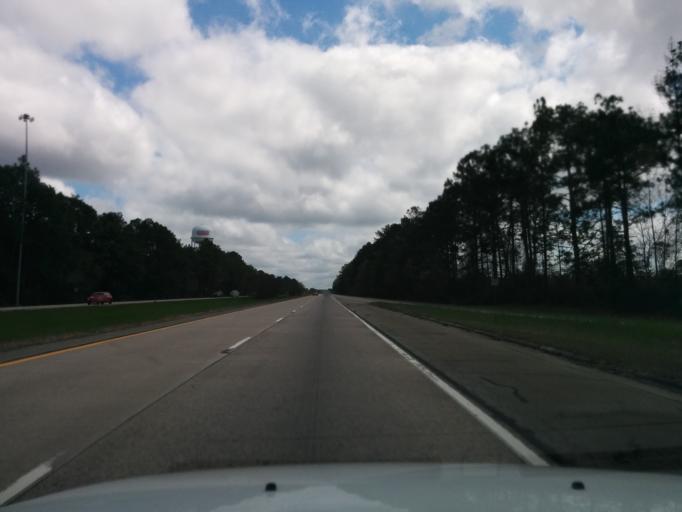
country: US
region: Georgia
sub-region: Chatham County
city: Bloomingdale
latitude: 32.1794
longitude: -81.4580
